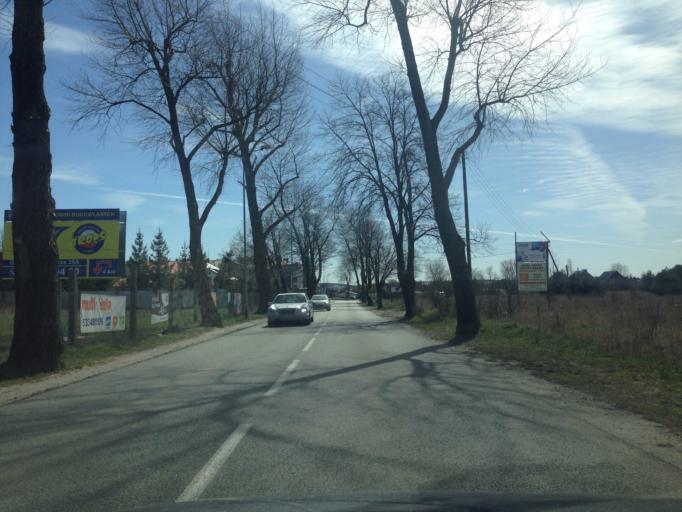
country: PL
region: Pomeranian Voivodeship
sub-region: Powiat wejherowski
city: Bojano
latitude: 54.4961
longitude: 18.4305
